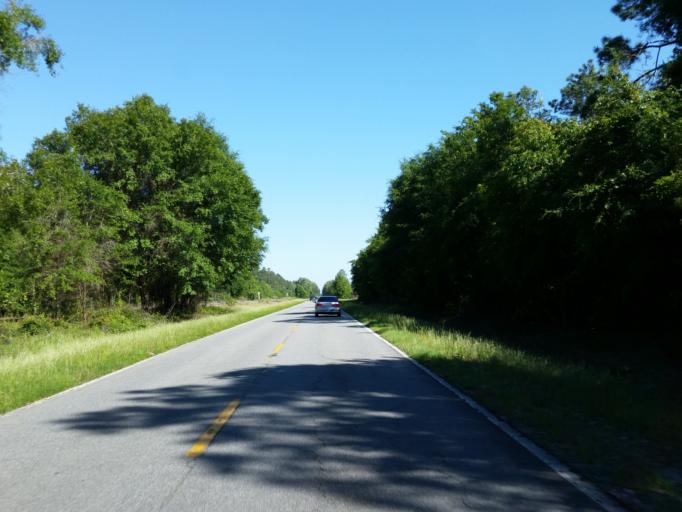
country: US
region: Georgia
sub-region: Echols County
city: Statenville
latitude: 30.6598
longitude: -83.1545
